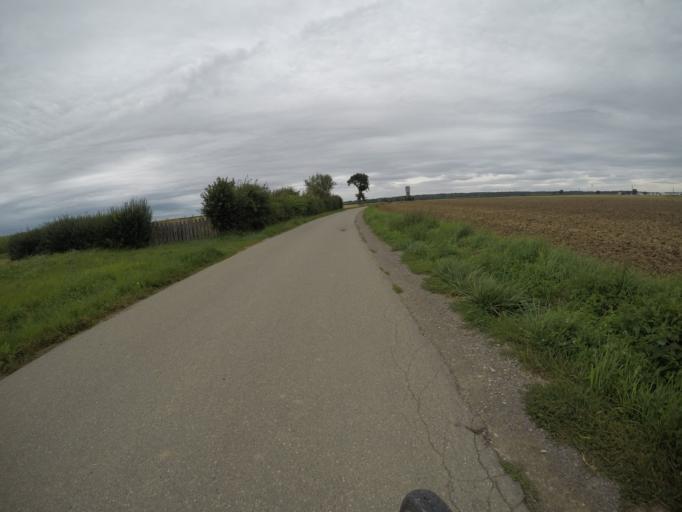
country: DE
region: Baden-Wuerttemberg
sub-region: Regierungsbezirk Stuttgart
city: Altdorf
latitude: 48.6348
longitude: 8.9938
